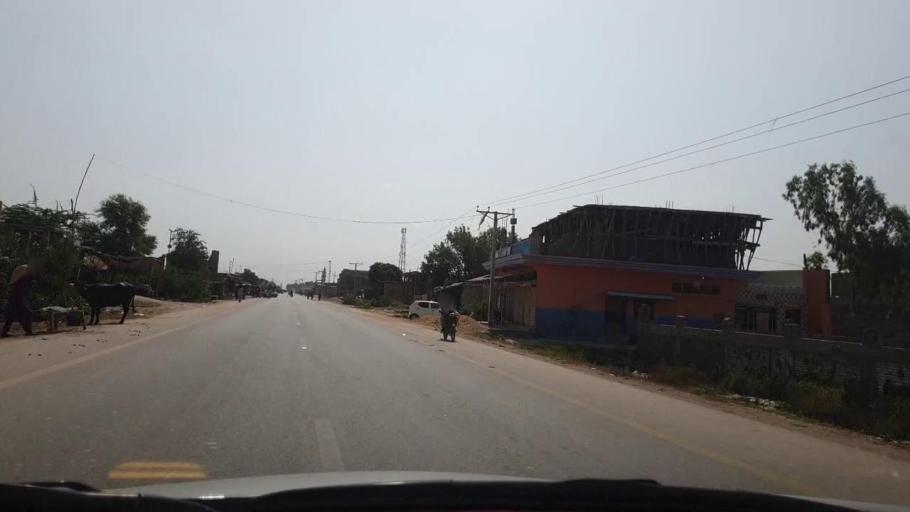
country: PK
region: Sindh
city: Matli
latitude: 25.0372
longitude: 68.6506
